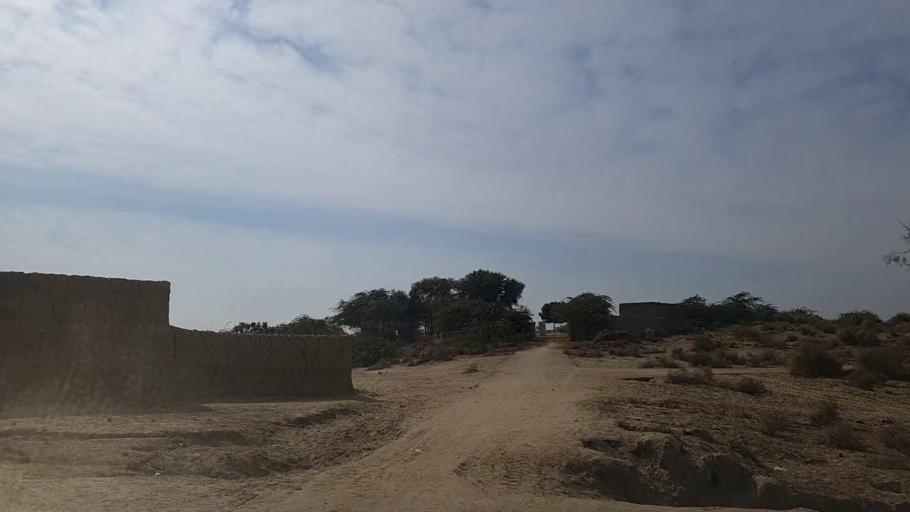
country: PK
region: Sindh
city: Nawabshah
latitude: 26.3737
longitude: 68.4447
